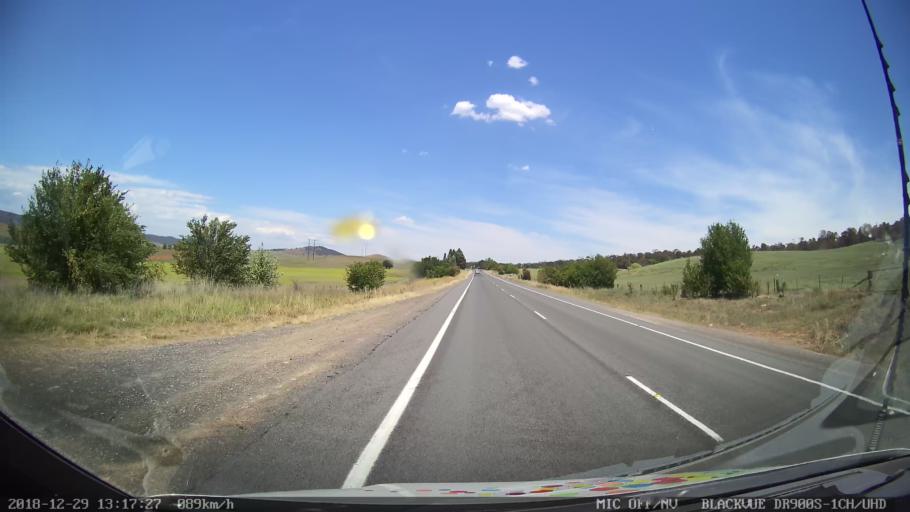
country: AU
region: Australian Capital Territory
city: Macarthur
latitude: -35.7377
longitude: 149.1607
